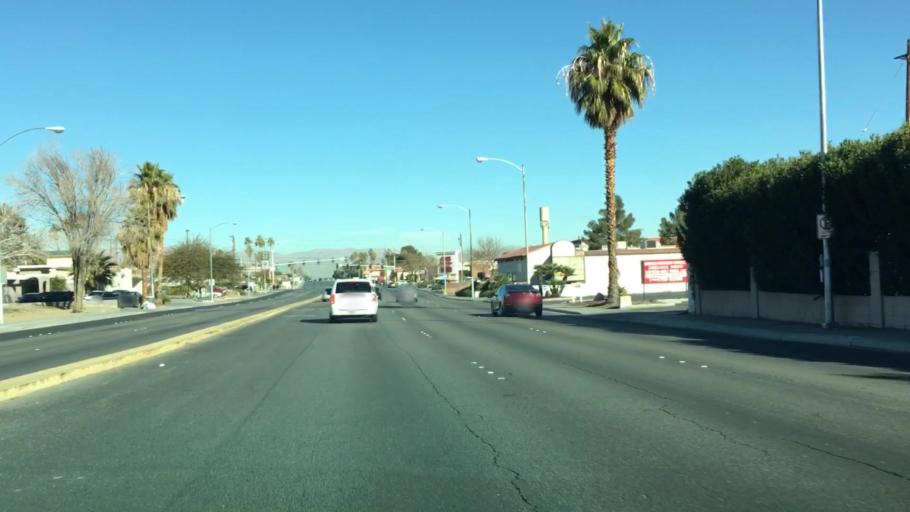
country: US
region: Nevada
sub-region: Clark County
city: Winchester
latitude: 36.1277
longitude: -115.1186
